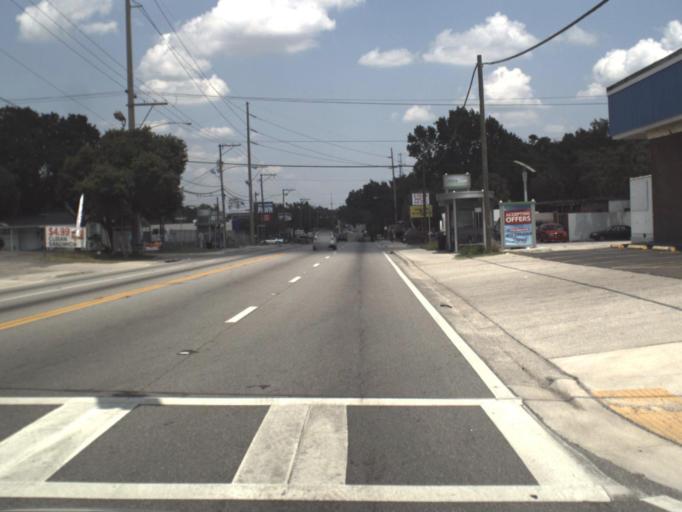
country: US
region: Florida
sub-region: Hillsborough County
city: Carrollwood
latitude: 28.0162
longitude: -82.4512
